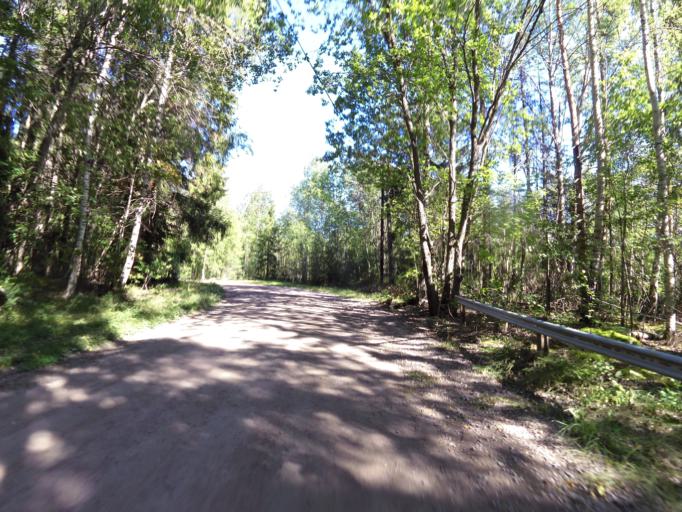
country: SE
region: Gaevleborg
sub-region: Hofors Kommun
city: Hofors
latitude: 60.5303
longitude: 16.4089
